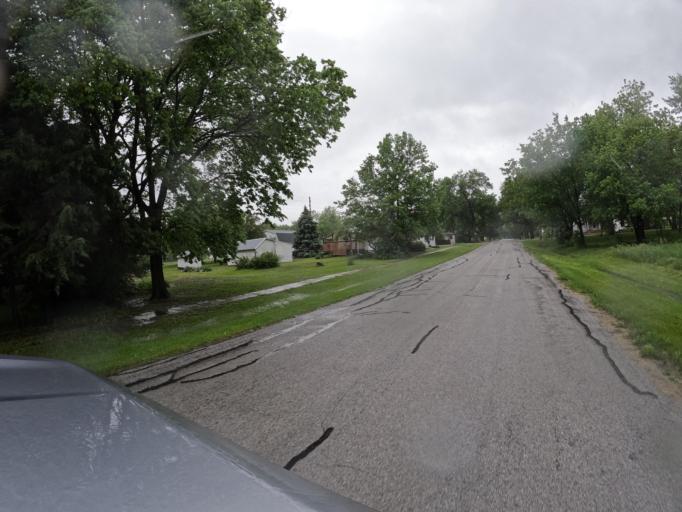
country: US
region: Nebraska
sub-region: Gage County
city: Wymore
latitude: 40.1385
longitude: -96.6591
